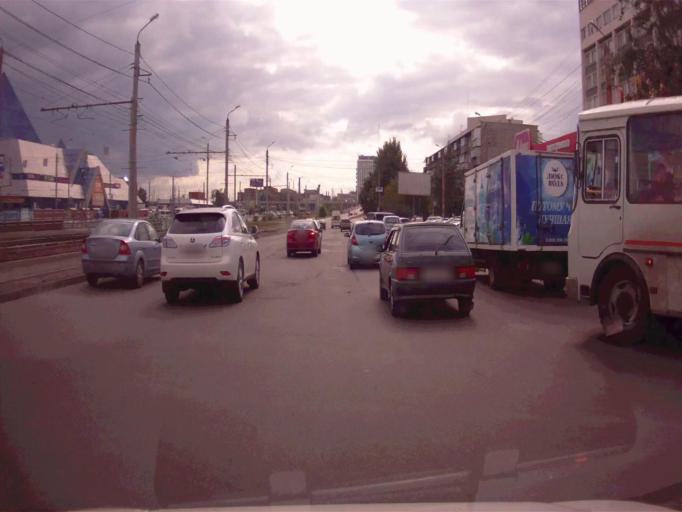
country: RU
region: Chelyabinsk
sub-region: Gorod Chelyabinsk
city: Chelyabinsk
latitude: 55.1417
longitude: 61.4126
